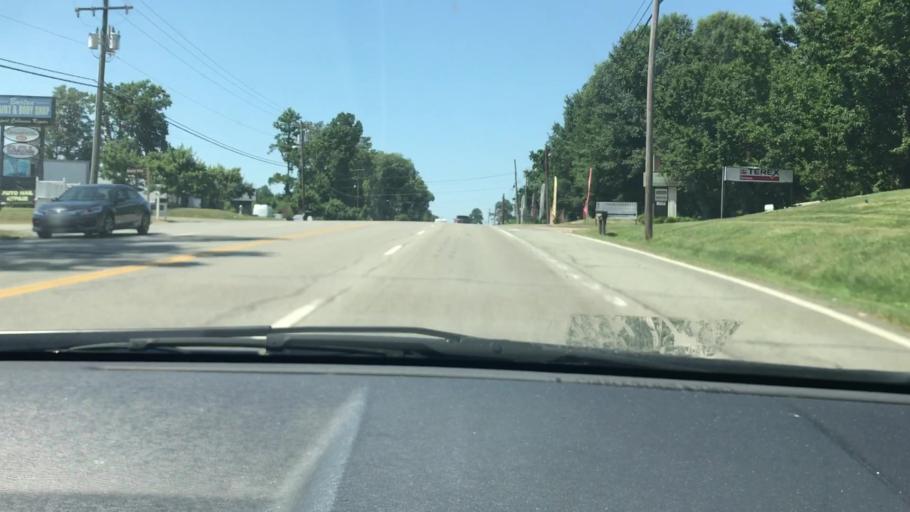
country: US
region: Virginia
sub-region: Henrico County
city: Glen Allen
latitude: 37.7029
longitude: -77.4647
